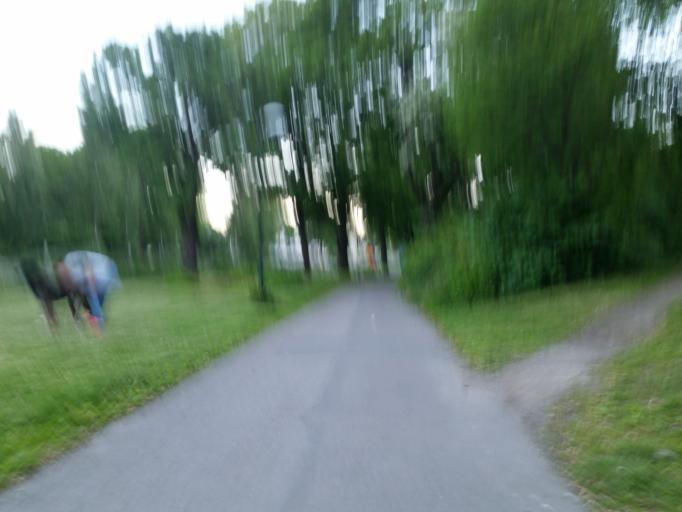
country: SE
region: Stockholm
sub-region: Stockholms Kommun
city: Arsta
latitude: 59.2974
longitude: 18.0714
